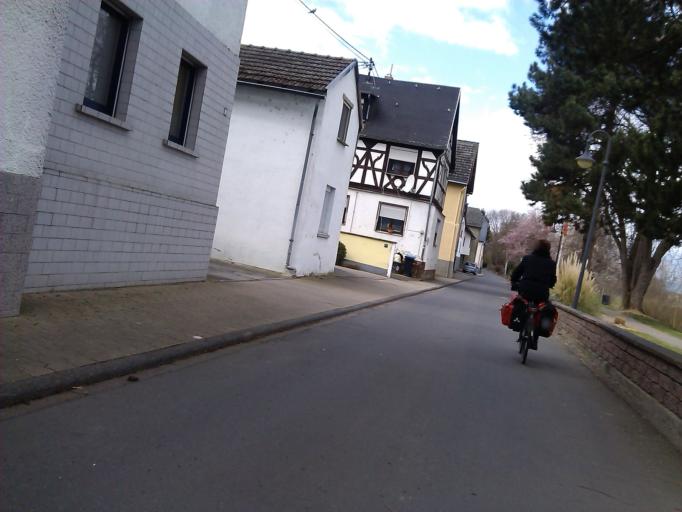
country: DE
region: Rheinland-Pfalz
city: Kaltenengers
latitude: 50.4173
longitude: 7.5451
